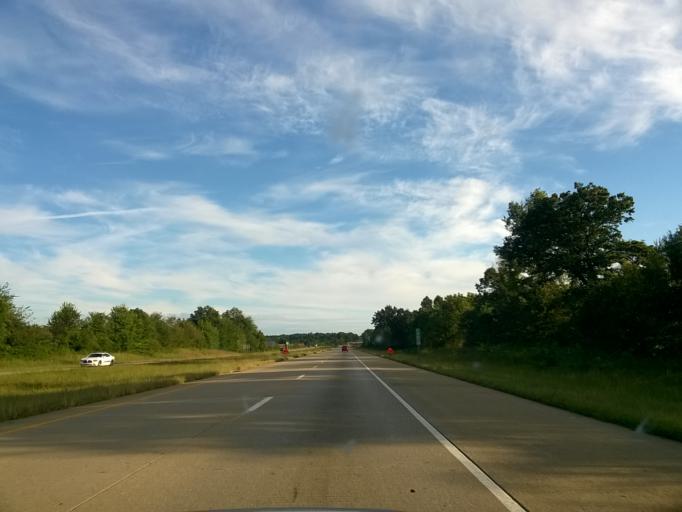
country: US
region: Indiana
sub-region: Gibson County
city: Haubstadt
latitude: 38.1581
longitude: -87.4724
